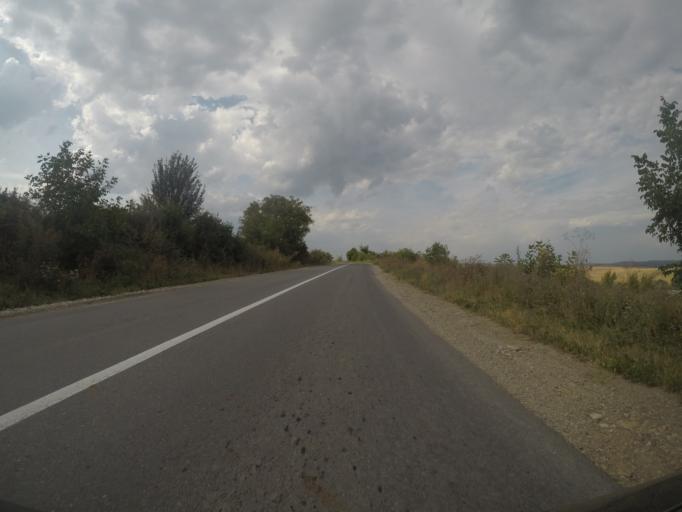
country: RO
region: Cluj
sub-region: Comuna Sandulesti
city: Copaceni
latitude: 46.5862
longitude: 23.7496
